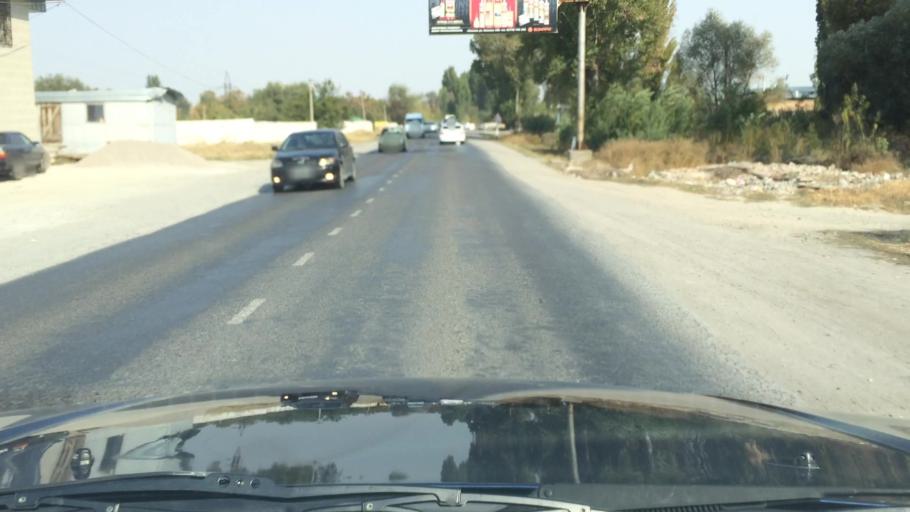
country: KG
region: Chuy
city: Lebedinovka
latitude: 42.8915
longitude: 74.6802
